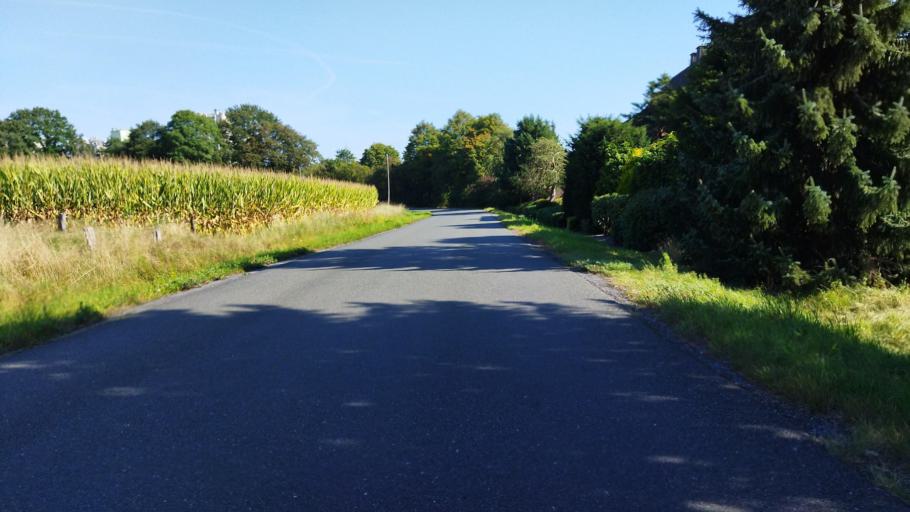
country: DE
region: North Rhine-Westphalia
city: Lengerich
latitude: 52.1665
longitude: 7.8882
